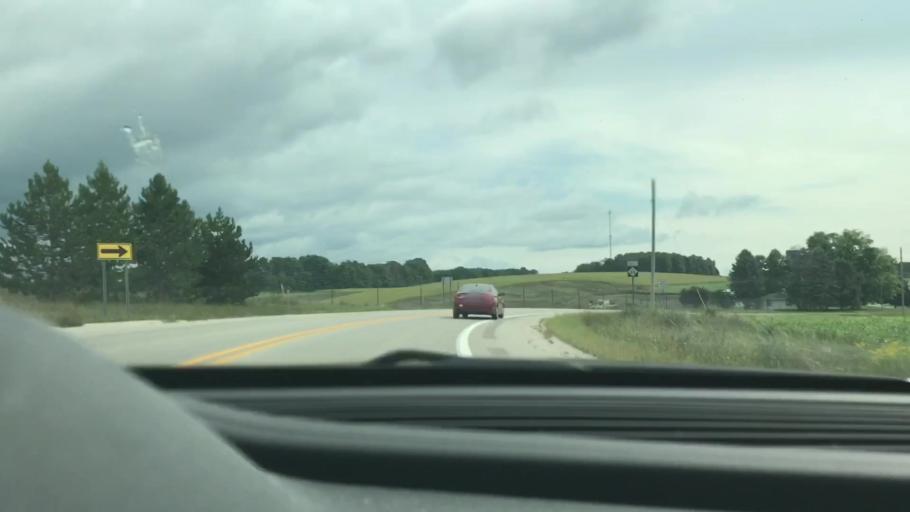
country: US
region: Michigan
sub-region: Antrim County
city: Bellaire
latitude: 45.0928
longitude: -85.2905
